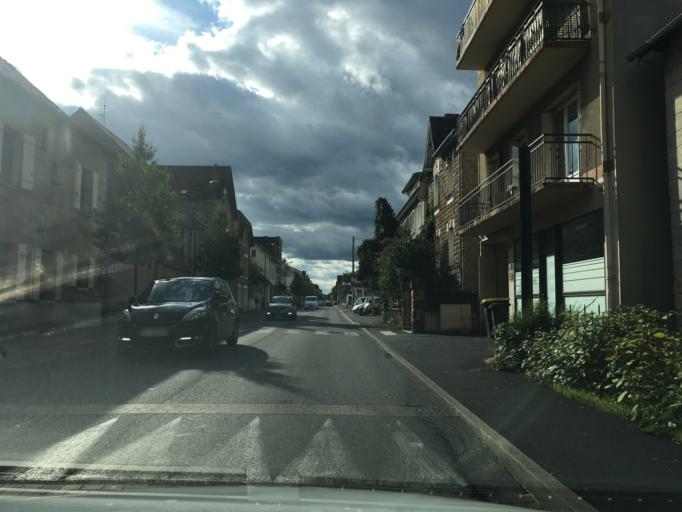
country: FR
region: Limousin
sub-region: Departement de la Correze
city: Brive-la-Gaillarde
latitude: 45.1577
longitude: 1.5470
